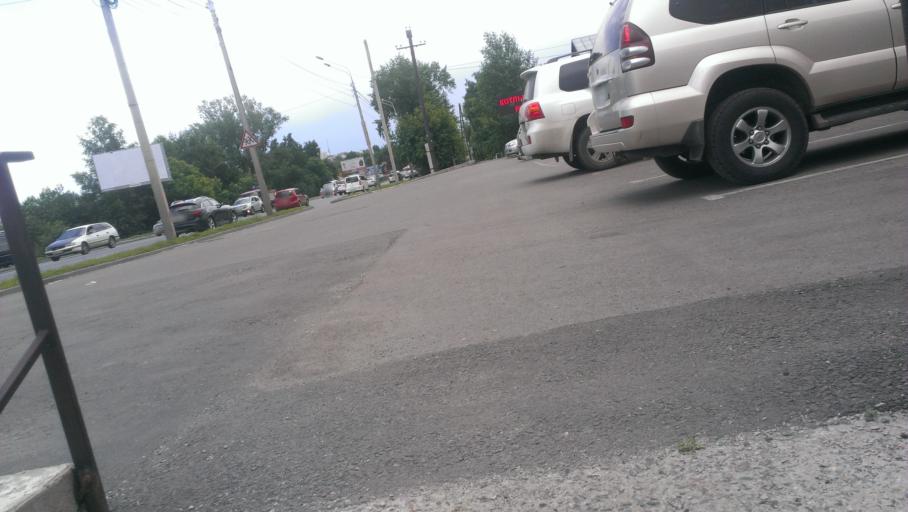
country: RU
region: Altai Krai
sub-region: Gorod Barnaulskiy
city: Barnaul
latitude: 53.3398
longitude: 83.7292
